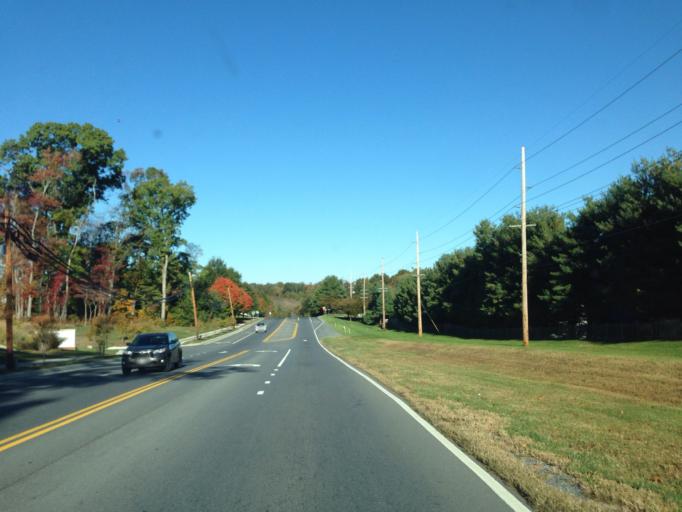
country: US
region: Maryland
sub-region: Montgomery County
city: Clarksburg
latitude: 39.2183
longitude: -77.2555
